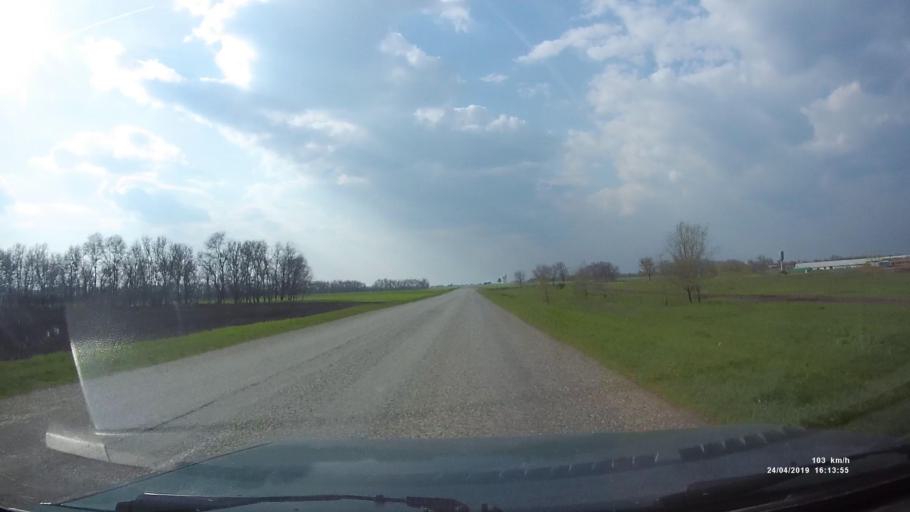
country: RU
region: Rostov
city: Sovetskoye
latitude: 46.7468
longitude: 42.2109
